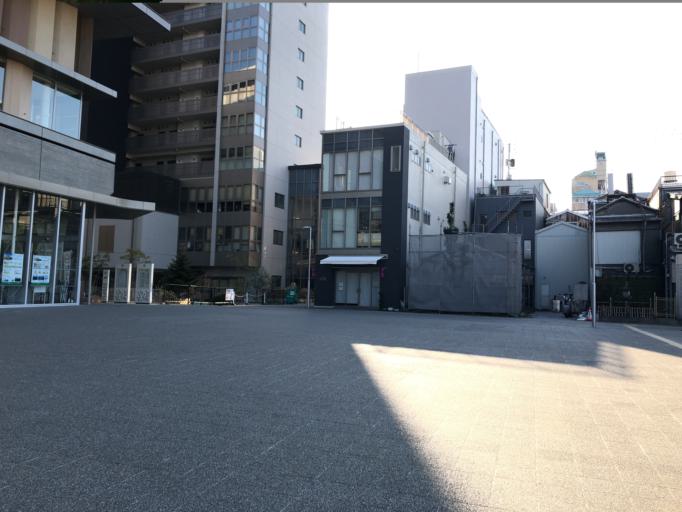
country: JP
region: Kochi
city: Kochi-shi
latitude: 33.5608
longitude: 133.5366
